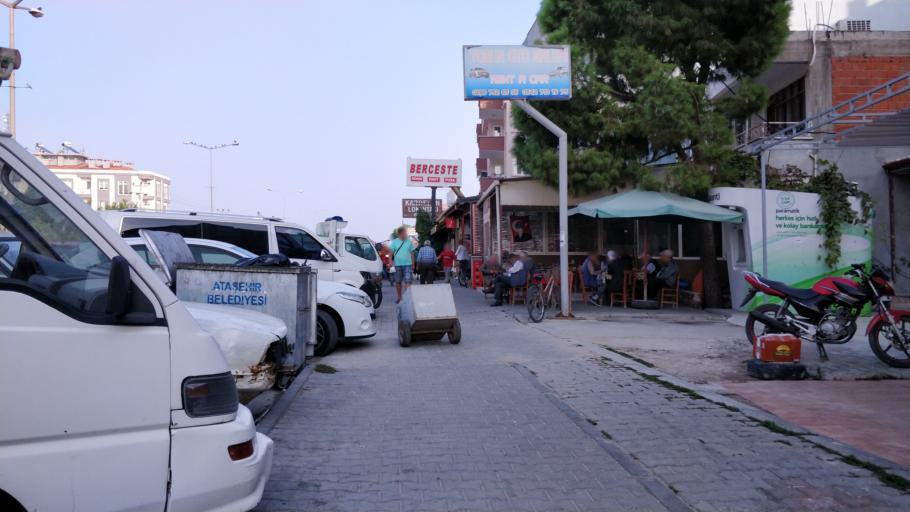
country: TR
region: Canakkale
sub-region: Merkez
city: Kucukkuyu
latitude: 39.5479
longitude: 26.6066
